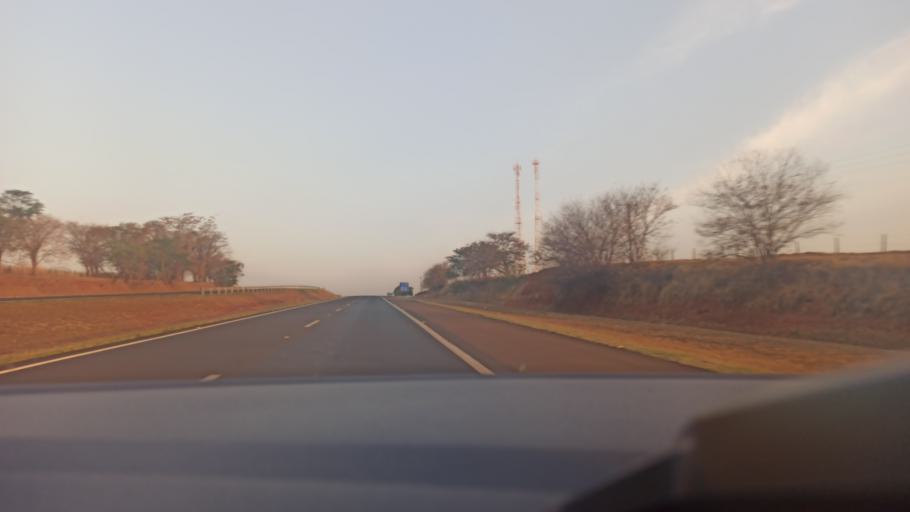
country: BR
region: Sao Paulo
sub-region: Taquaritinga
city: Taquaritinga
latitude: -21.4206
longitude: -48.6783
